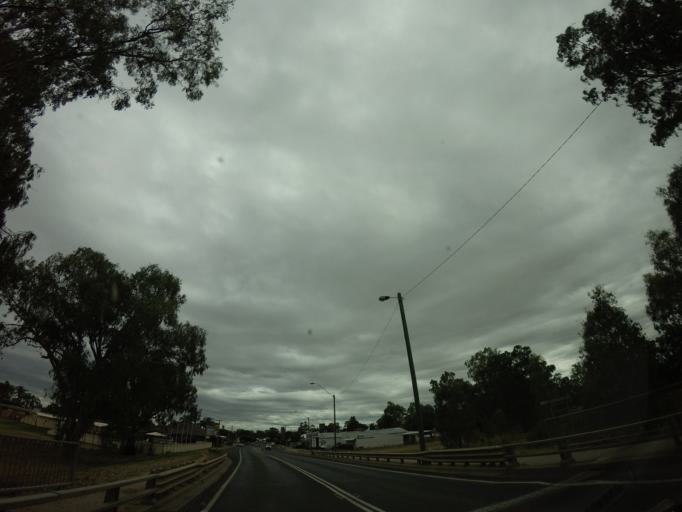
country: AU
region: New South Wales
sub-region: Narrabri
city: Narrabri
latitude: -30.3315
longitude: 149.7746
